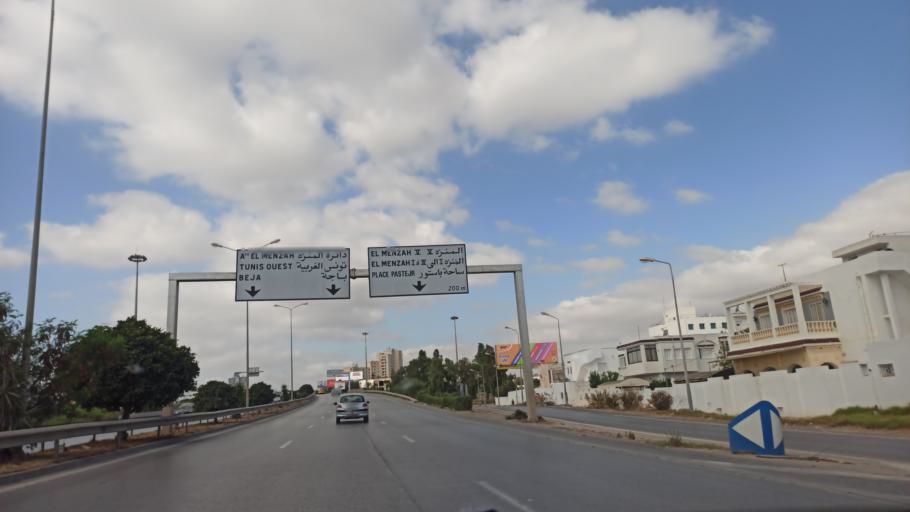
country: TN
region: Ariana
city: Ariana
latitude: 36.8490
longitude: 10.1853
